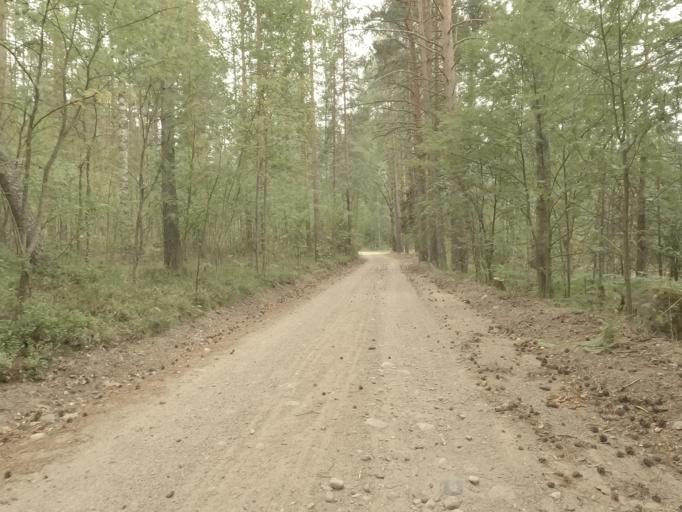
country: RU
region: Leningrad
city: Kamennogorsk
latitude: 60.9972
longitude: 29.1829
